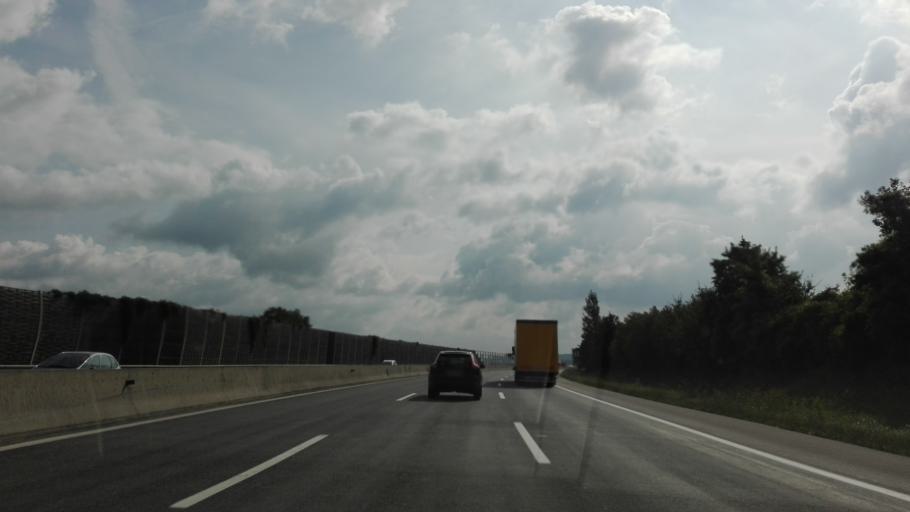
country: AT
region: Lower Austria
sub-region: Politischer Bezirk Melk
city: Melk
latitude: 48.2174
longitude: 15.3238
